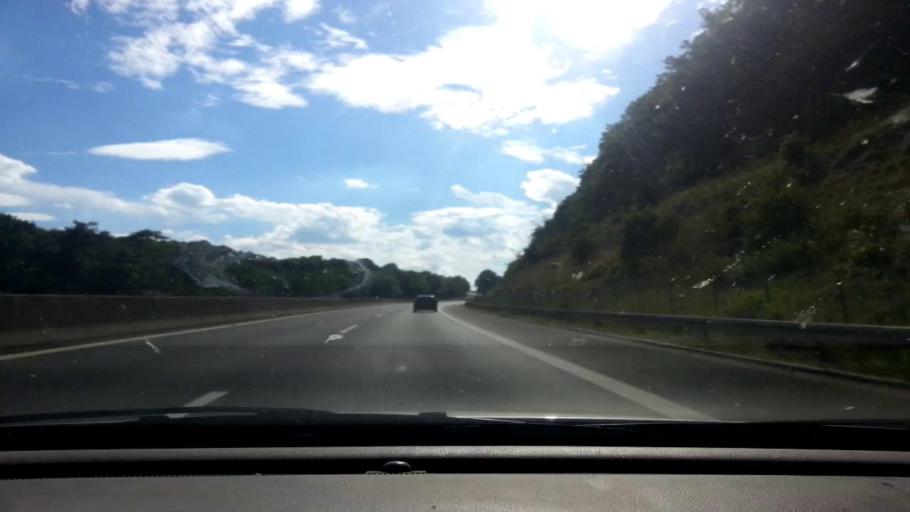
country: DE
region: Bavaria
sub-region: Upper Franconia
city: Kasendorf
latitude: 50.0110
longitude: 11.3666
